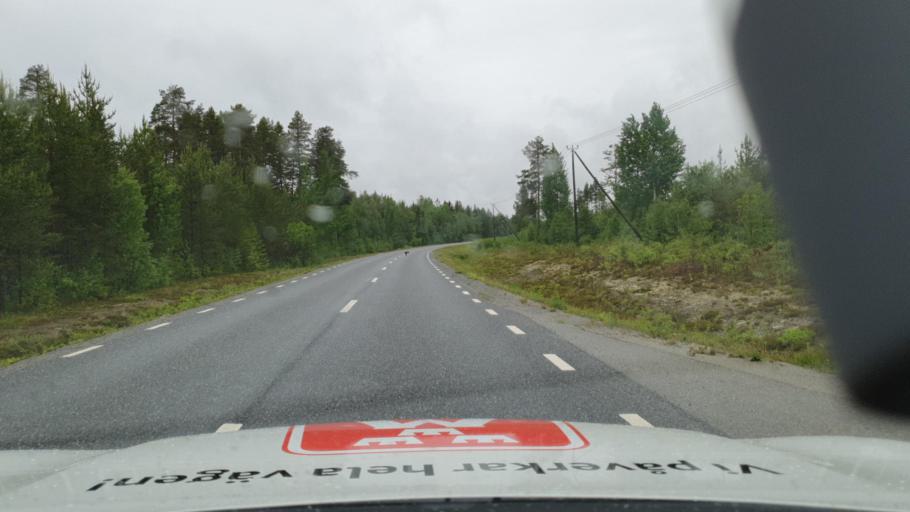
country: SE
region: Vaesterbotten
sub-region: Asele Kommun
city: Asele
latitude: 63.9687
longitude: 17.2641
